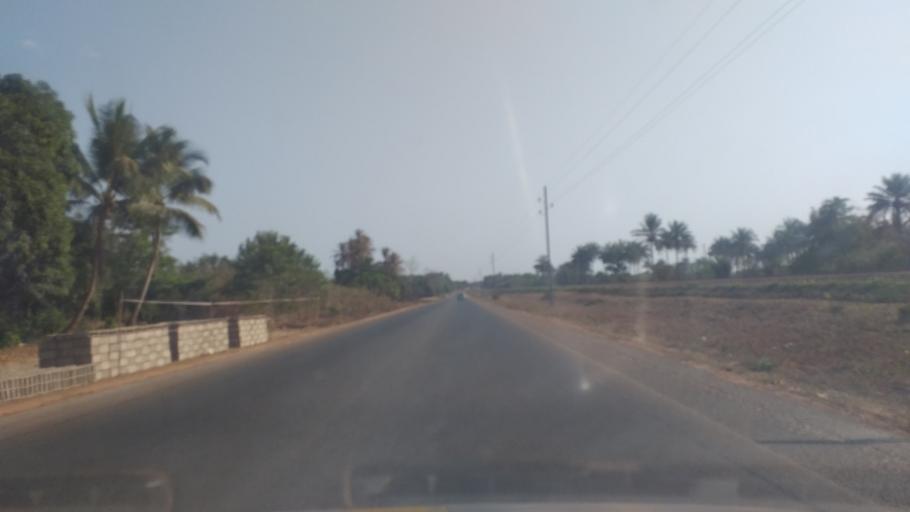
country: GN
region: Boke
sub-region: Boke Prefecture
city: Kamsar
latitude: 10.7269
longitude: -14.5186
